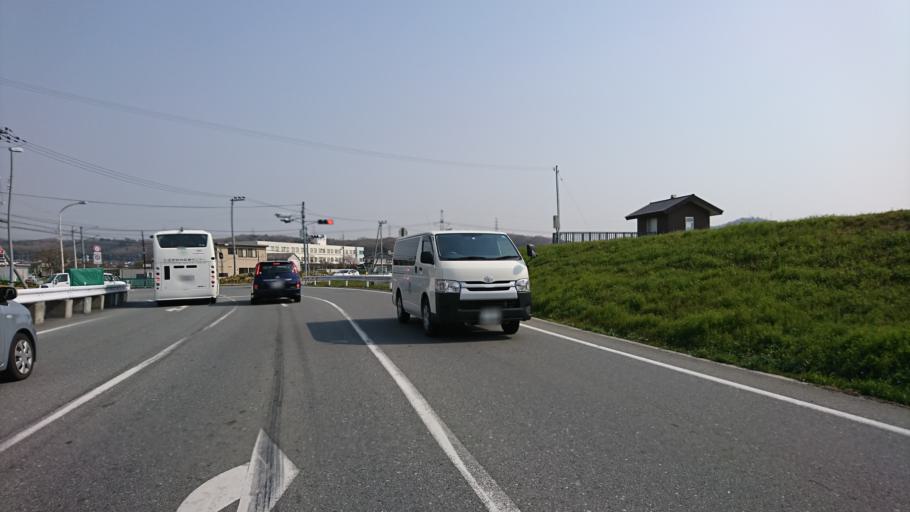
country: JP
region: Hyogo
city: Ono
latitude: 34.8227
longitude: 134.9373
